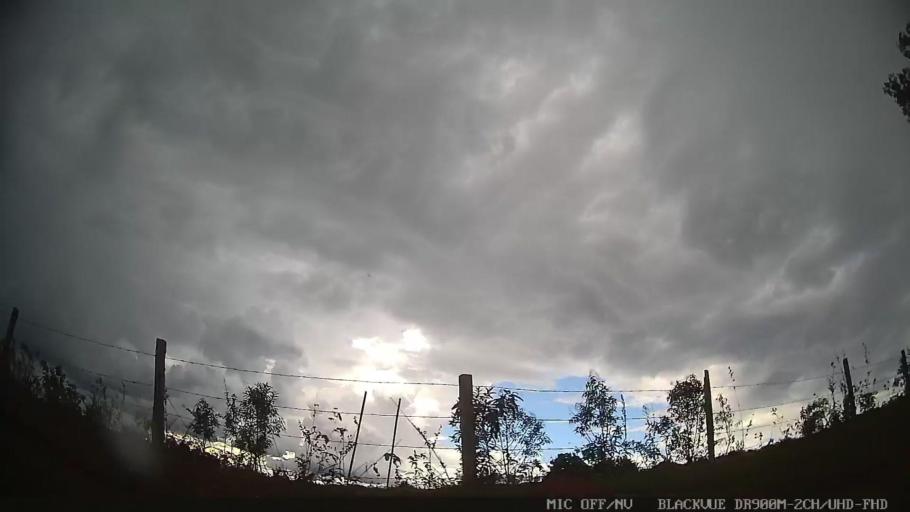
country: BR
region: Sao Paulo
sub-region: Pedreira
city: Pedreira
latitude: -22.7128
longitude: -46.8878
